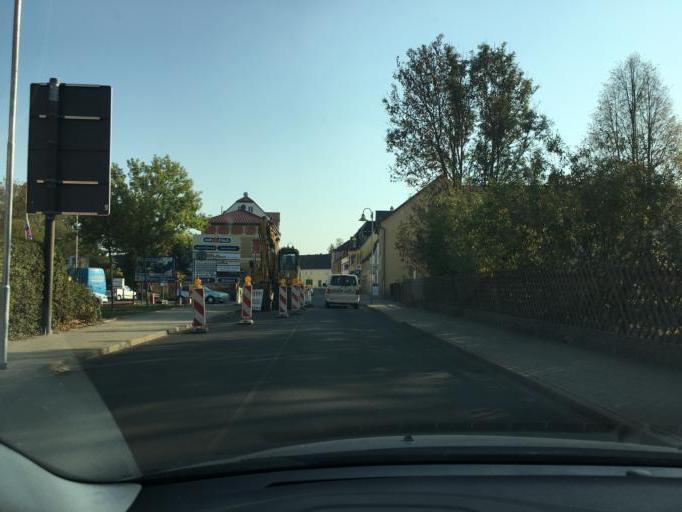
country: DE
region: Saxony
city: Wermsdorf
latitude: 51.2823
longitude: 12.9411
